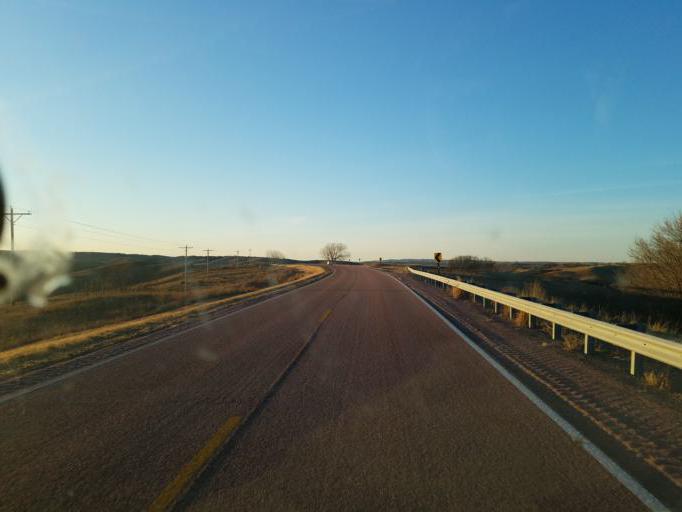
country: US
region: South Dakota
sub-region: Bon Homme County
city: Springfield
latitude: 42.7406
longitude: -97.9142
